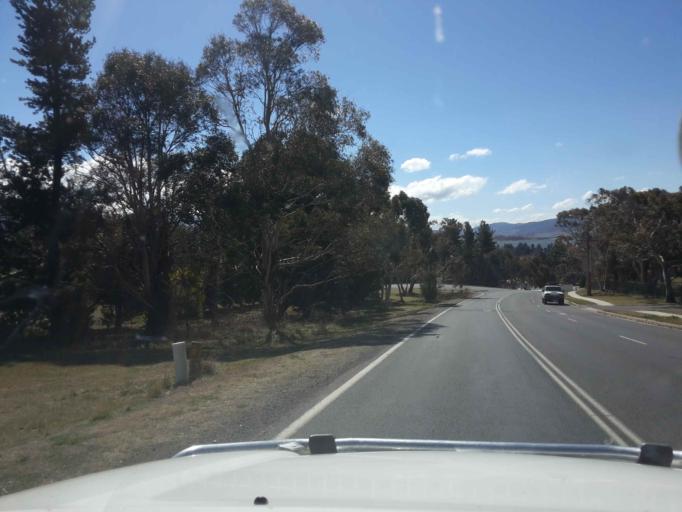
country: AU
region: New South Wales
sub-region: Snowy River
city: Jindabyne
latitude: -36.4189
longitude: 148.6104
